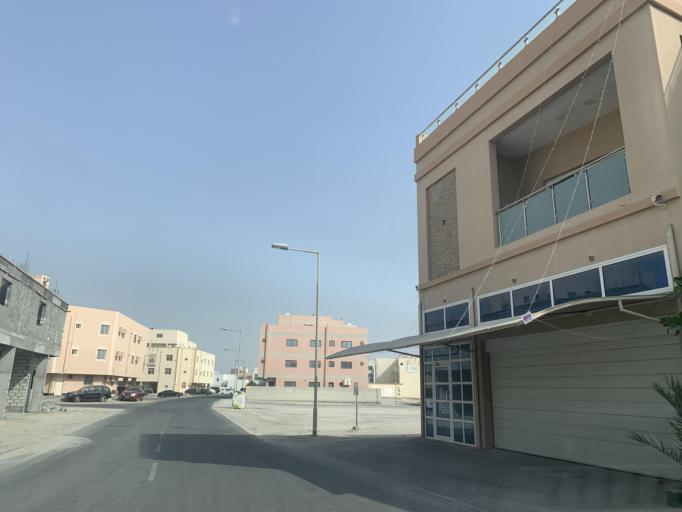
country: BH
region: Northern
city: Madinat `Isa
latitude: 26.1874
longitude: 50.5606
